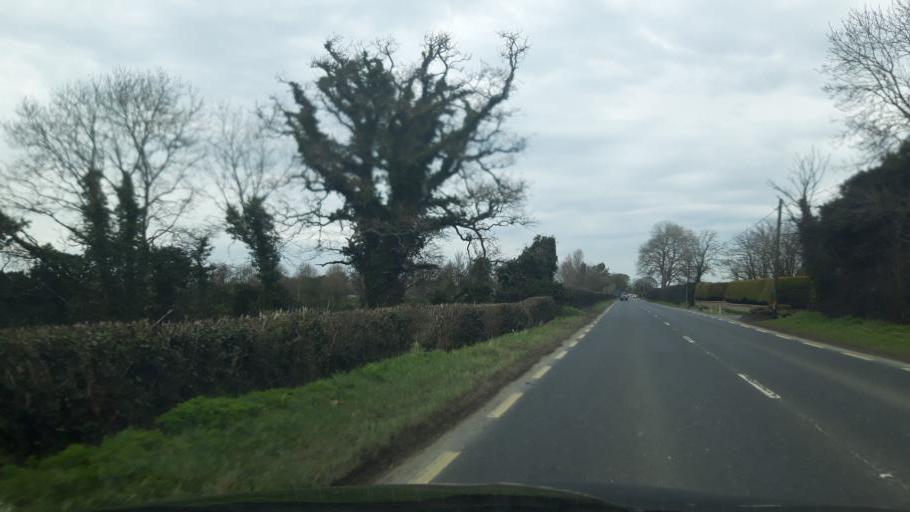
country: IE
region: Leinster
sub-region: Kildare
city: Maynooth
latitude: 53.3557
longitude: -6.5954
